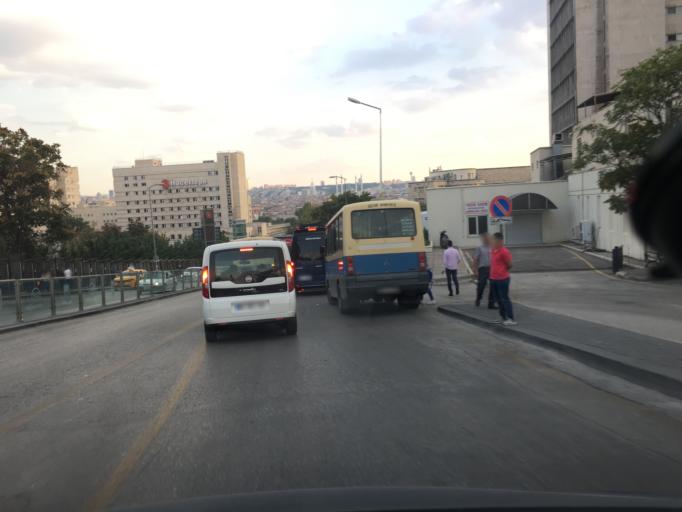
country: TR
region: Ankara
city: Ankara
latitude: 39.9326
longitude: 32.8598
